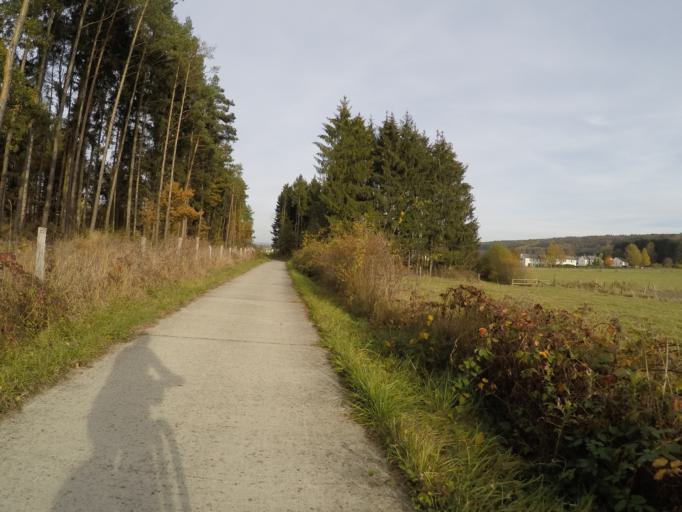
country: BE
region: Wallonia
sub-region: Province du Luxembourg
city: Marche-en-Famenne
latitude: 50.2434
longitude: 5.3760
